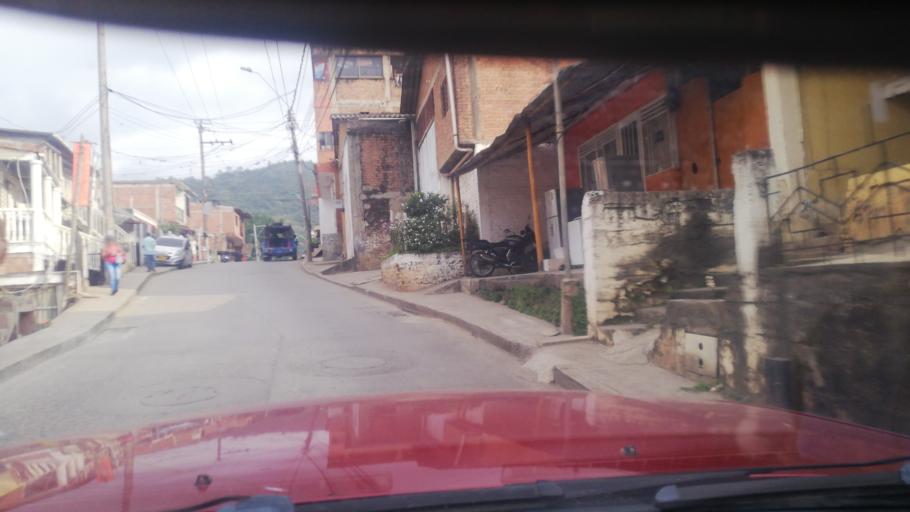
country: CO
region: Valle del Cauca
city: Cali
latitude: 3.4835
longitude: -76.5528
